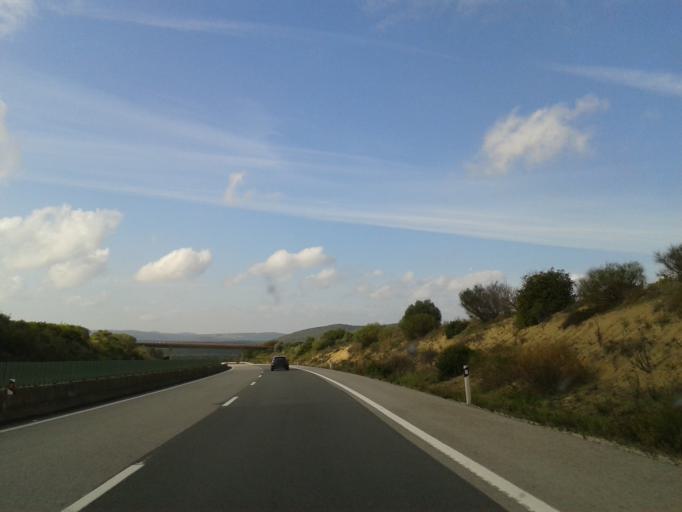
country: PT
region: Faro
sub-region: Tavira
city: Luz
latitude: 37.1376
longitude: -7.7351
